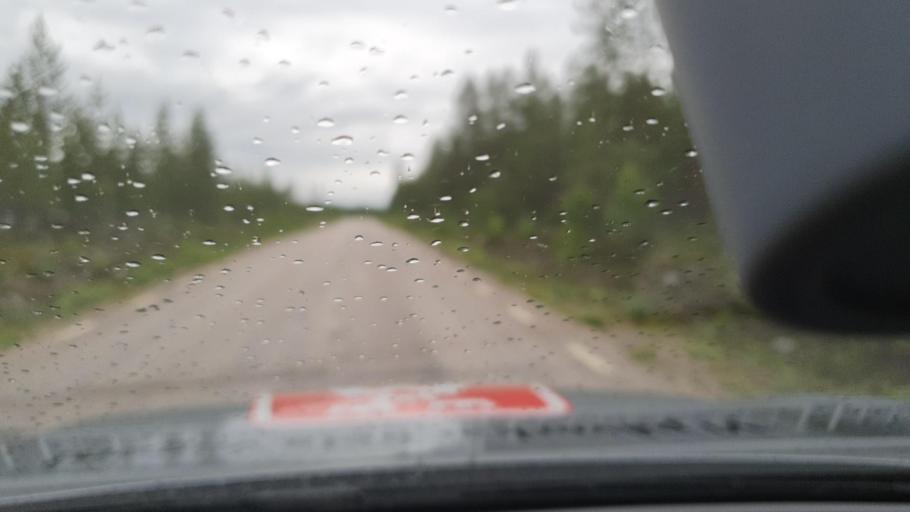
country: SE
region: Norrbotten
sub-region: Overkalix Kommun
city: OEverkalix
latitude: 66.3765
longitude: 22.7964
